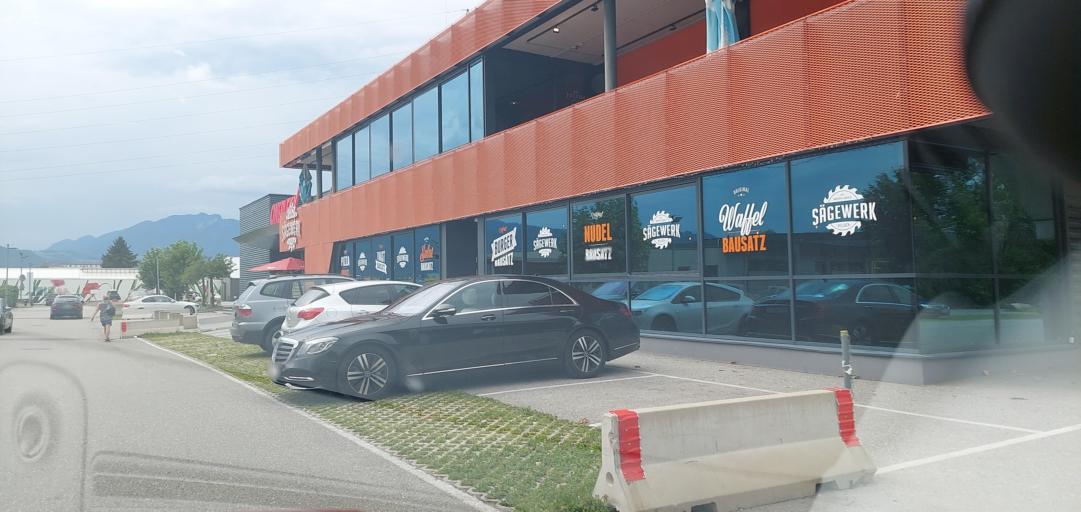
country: AT
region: Carinthia
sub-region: Villach Stadt
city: Villach
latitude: 46.6057
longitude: 13.8670
